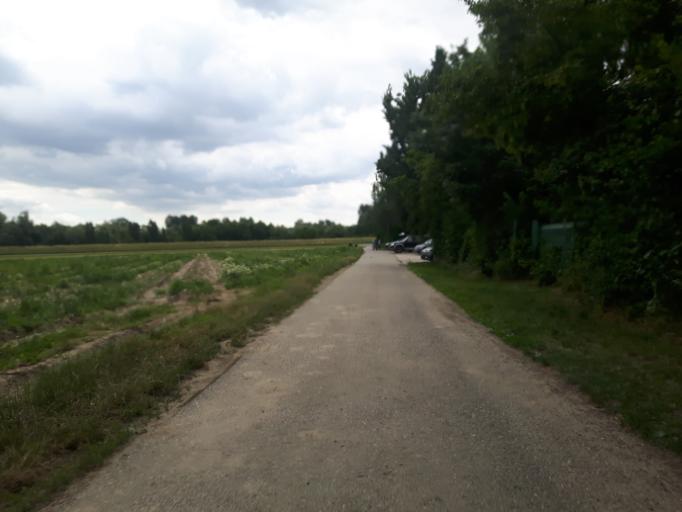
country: DE
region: Rheinland-Pfalz
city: Otterstadt
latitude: 49.3820
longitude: 8.4542
